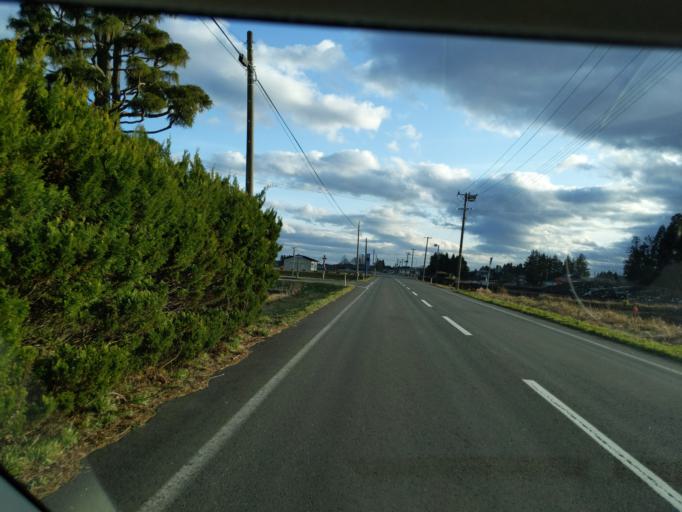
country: JP
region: Iwate
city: Mizusawa
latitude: 39.1387
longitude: 141.0509
